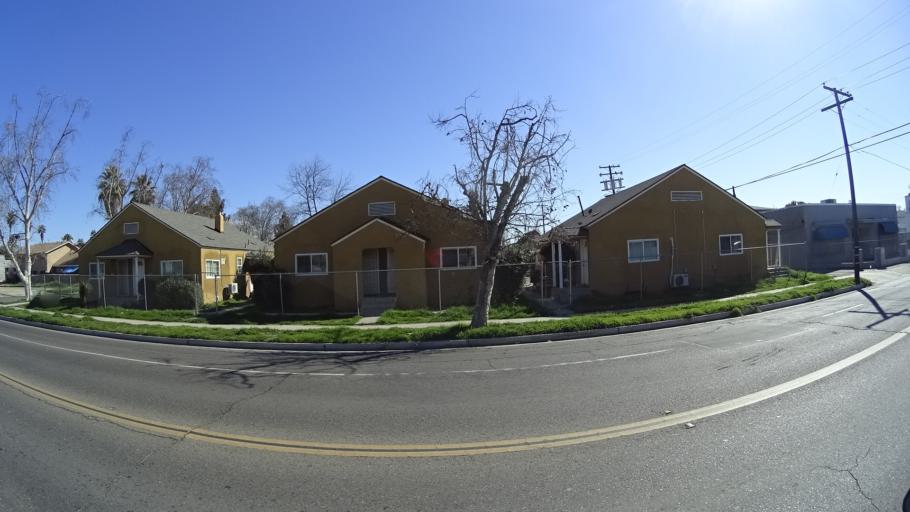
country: US
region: California
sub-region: Fresno County
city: Fresno
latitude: 36.7523
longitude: -119.7816
